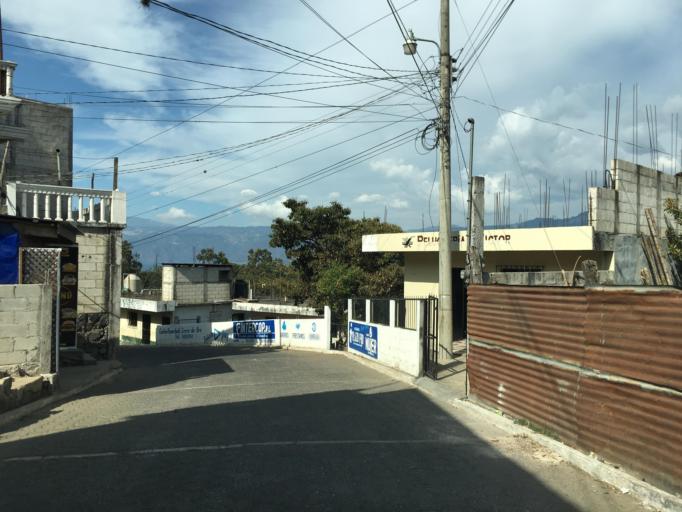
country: GT
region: Solola
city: San Antonio Palopo
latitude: 14.6612
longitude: -91.1617
